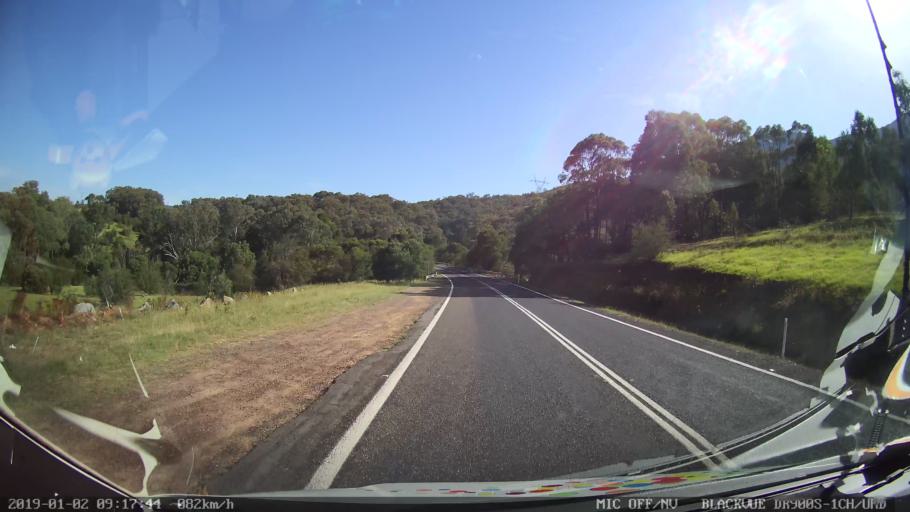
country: AU
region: New South Wales
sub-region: Tumut Shire
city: Tumut
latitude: -35.4365
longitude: 148.2870
